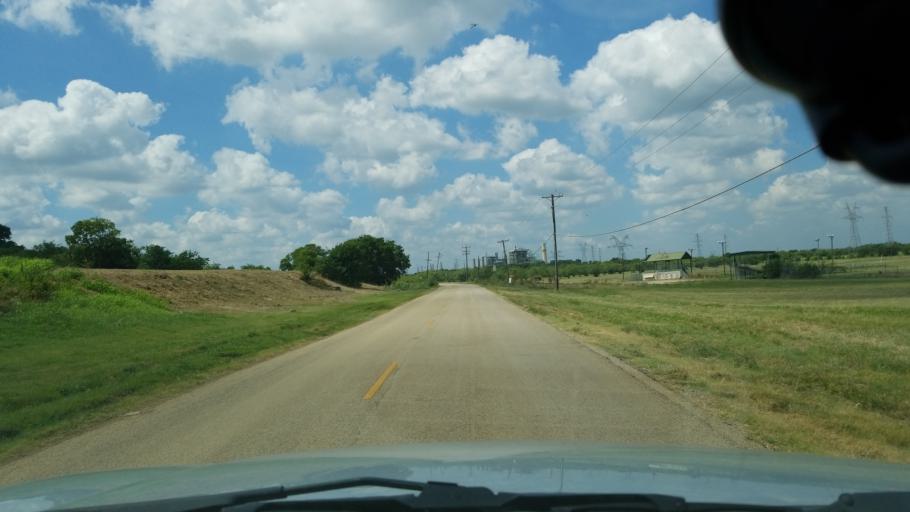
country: US
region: Texas
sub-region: Dallas County
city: Cockrell Hill
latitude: 32.7365
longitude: -96.9301
